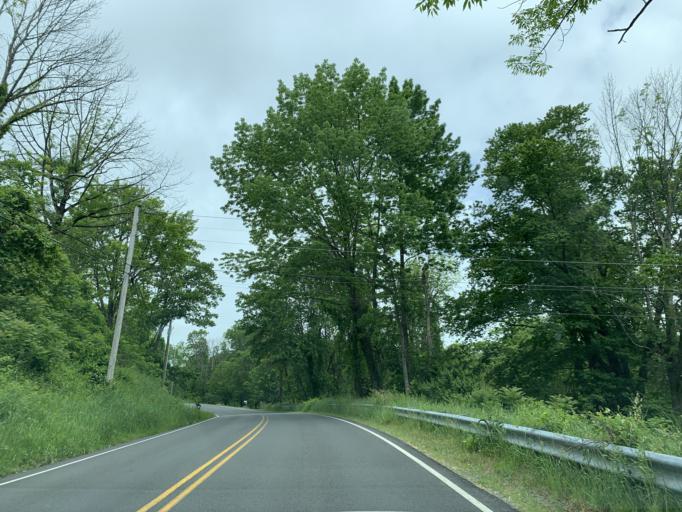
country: US
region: Massachusetts
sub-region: Hampshire County
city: Southampton
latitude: 42.2009
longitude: -72.7934
